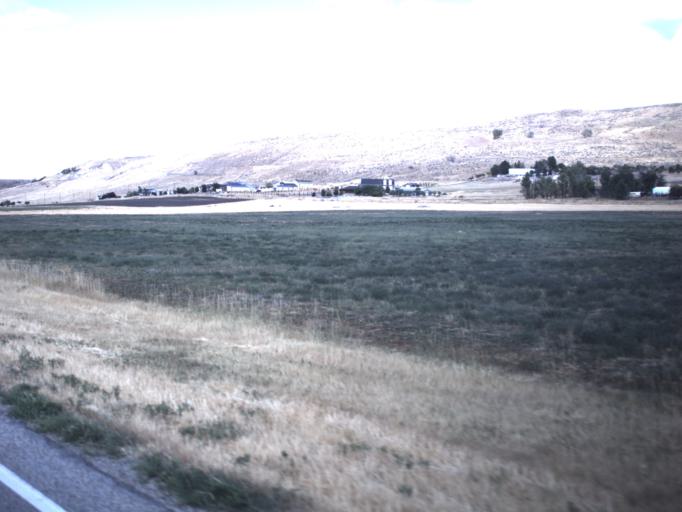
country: US
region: Utah
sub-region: Box Elder County
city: Garland
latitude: 41.7587
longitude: -112.0980
